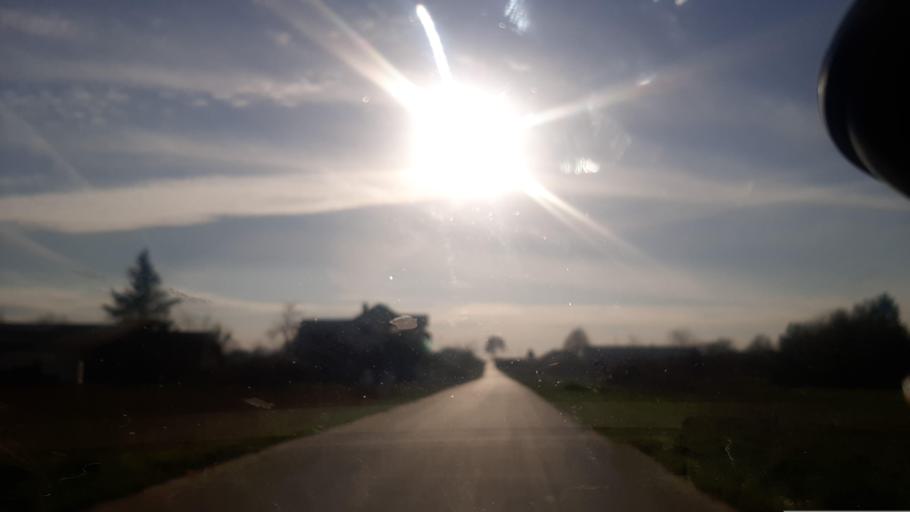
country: PL
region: Lublin Voivodeship
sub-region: Powiat lubelski
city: Garbow
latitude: 51.3889
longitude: 22.3441
